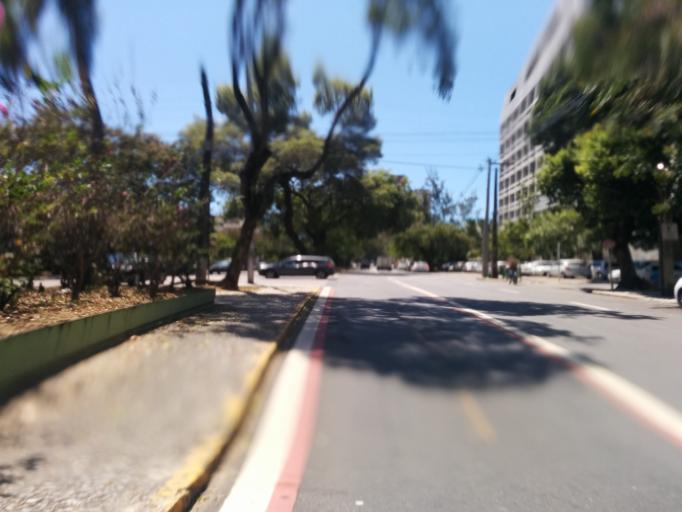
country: BR
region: Pernambuco
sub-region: Recife
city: Recife
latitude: -8.0517
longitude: -34.8849
